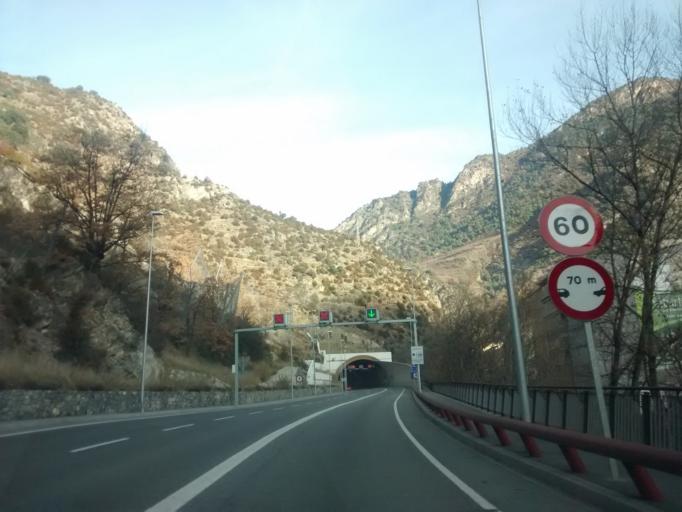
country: AD
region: Sant Julia de Loria
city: Sant Julia de Loria
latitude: 42.4678
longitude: 1.4916
